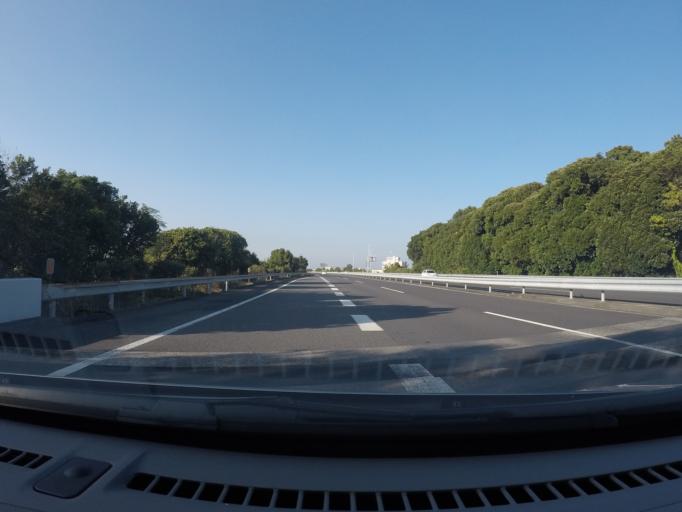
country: JP
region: Kagoshima
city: Hamanoichi
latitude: 31.7898
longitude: 130.7174
